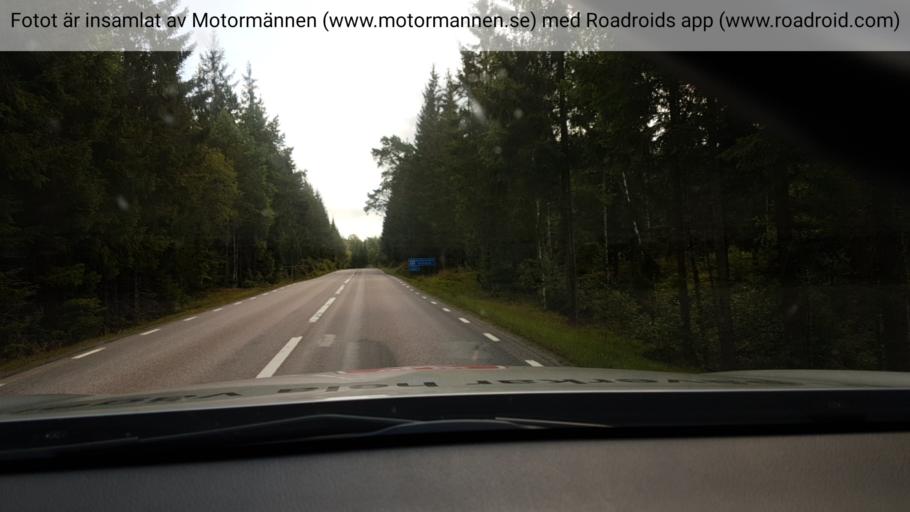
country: SE
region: Vaestra Goetaland
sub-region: Marks Kommun
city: Fritsla
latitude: 57.4914
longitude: 12.8786
